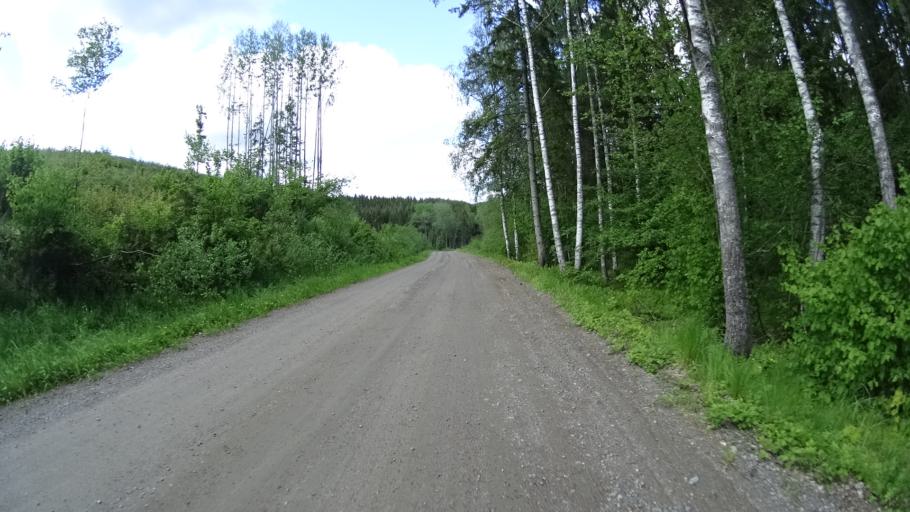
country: FI
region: Uusimaa
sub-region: Raaseporin
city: Pohja
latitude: 60.1610
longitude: 23.6061
